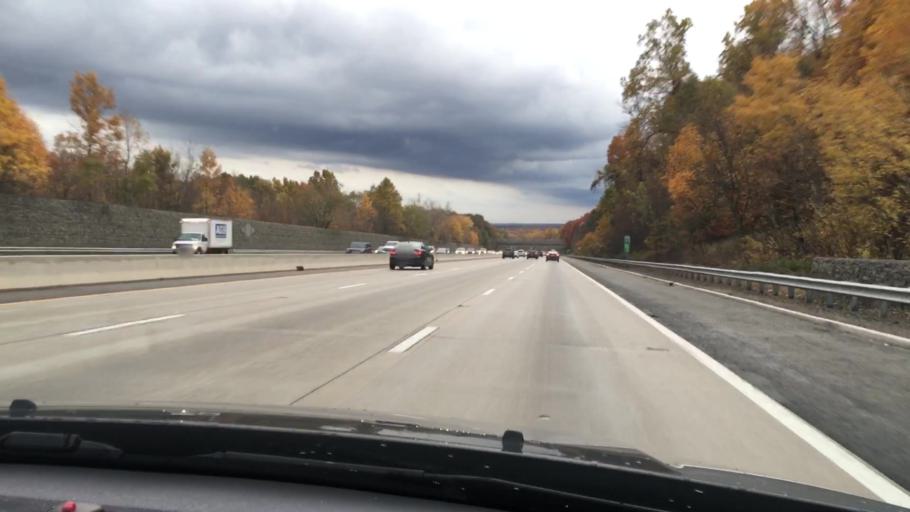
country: US
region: New Jersey
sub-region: Morris County
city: Lincoln Park
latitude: 40.9542
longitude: -74.3405
